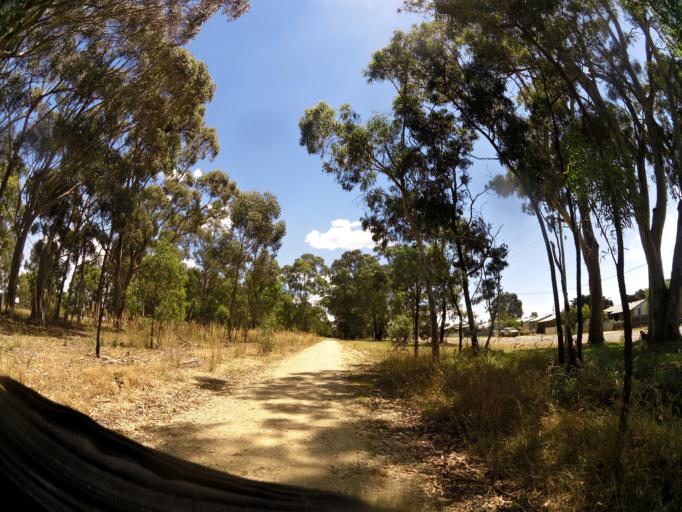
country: AU
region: Victoria
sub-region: Wellington
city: Heyfield
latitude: -37.9802
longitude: 146.7959
